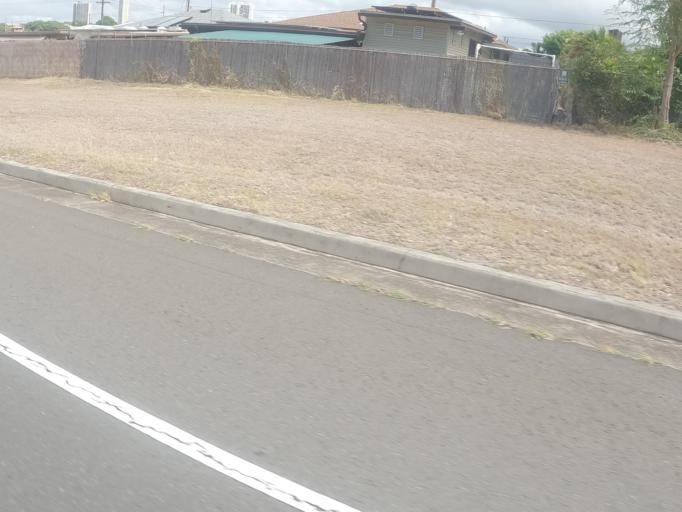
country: US
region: Hawaii
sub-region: Honolulu County
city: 'Aiea
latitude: 21.3761
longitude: -157.9321
